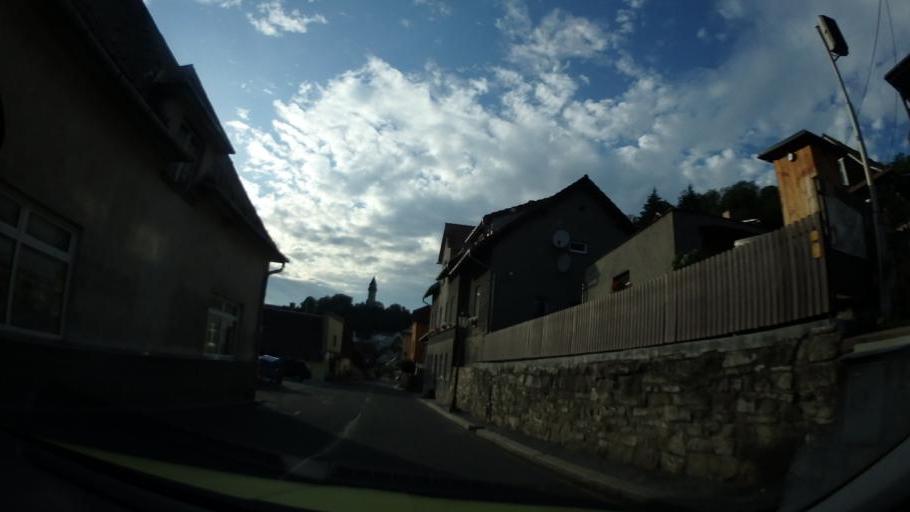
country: CZ
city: Stramberk
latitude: 49.5887
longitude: 18.1215
